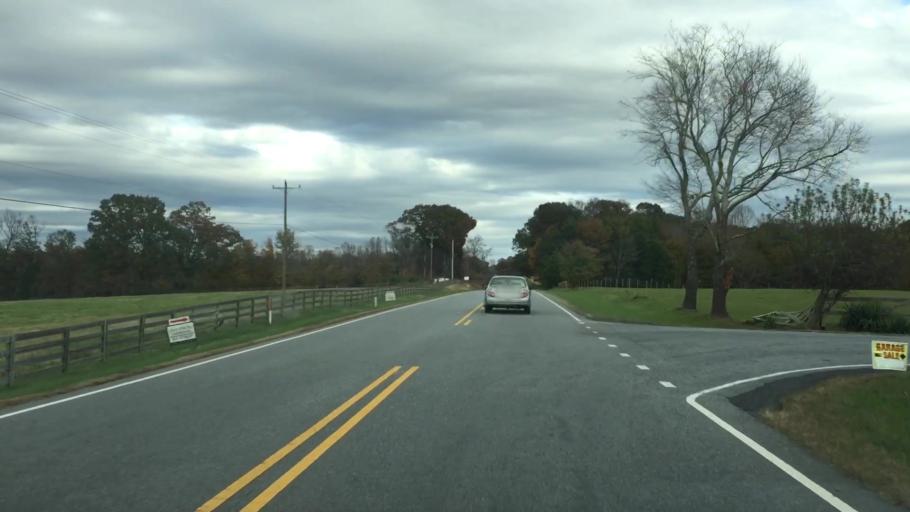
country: US
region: North Carolina
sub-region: Guilford County
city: Summerfield
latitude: 36.2737
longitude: -79.8254
